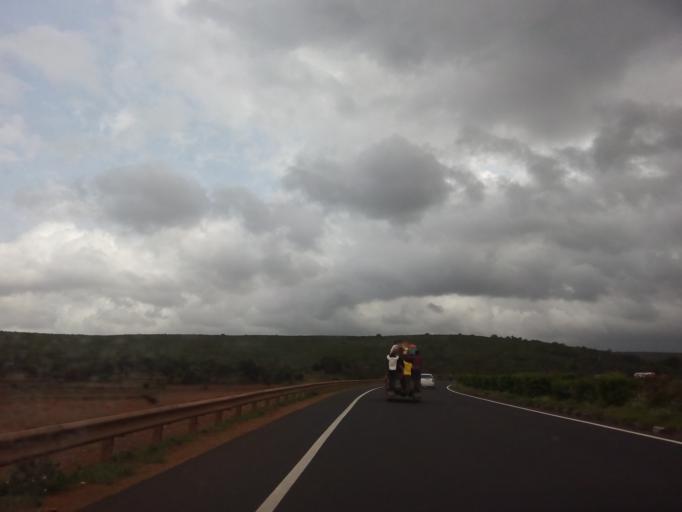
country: IN
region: Karnataka
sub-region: Belgaum
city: Hukeri
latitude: 16.0692
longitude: 74.5184
